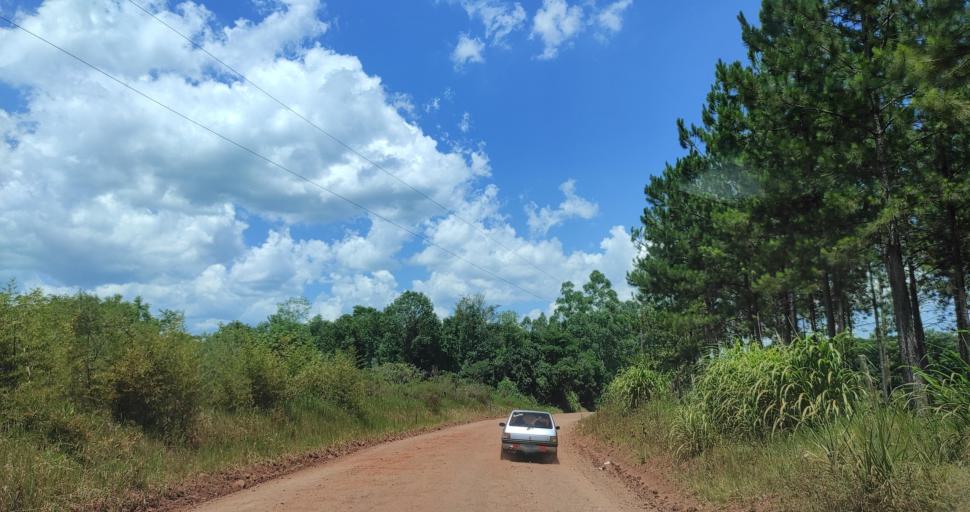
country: AR
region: Misiones
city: Ruiz de Montoya
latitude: -27.0426
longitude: -55.0127
